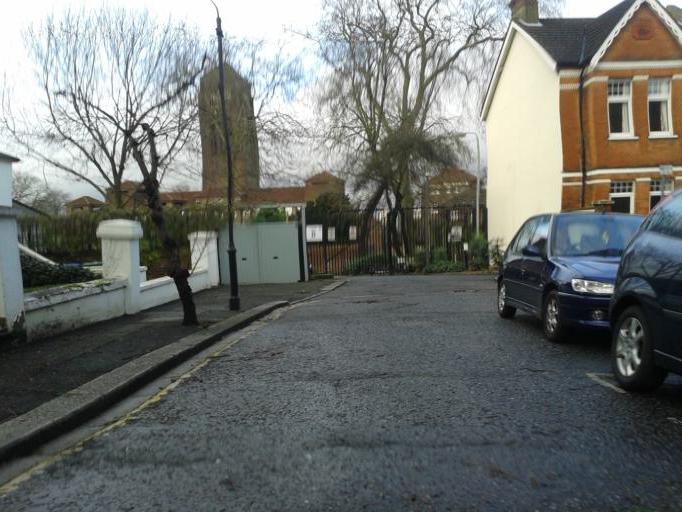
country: GB
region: England
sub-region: Greater London
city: Camberwell
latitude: 51.4665
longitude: -0.0869
